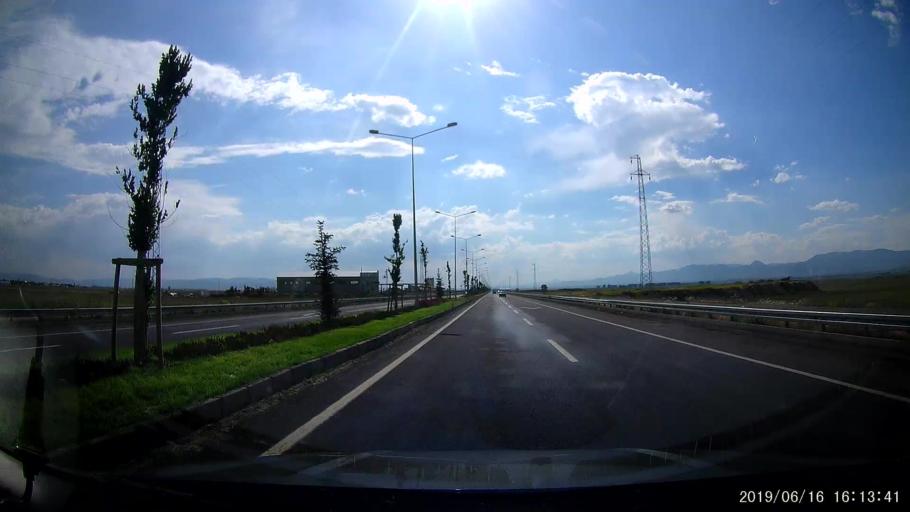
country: TR
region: Erzurum
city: Erzurum
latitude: 39.9598
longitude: 41.2658
